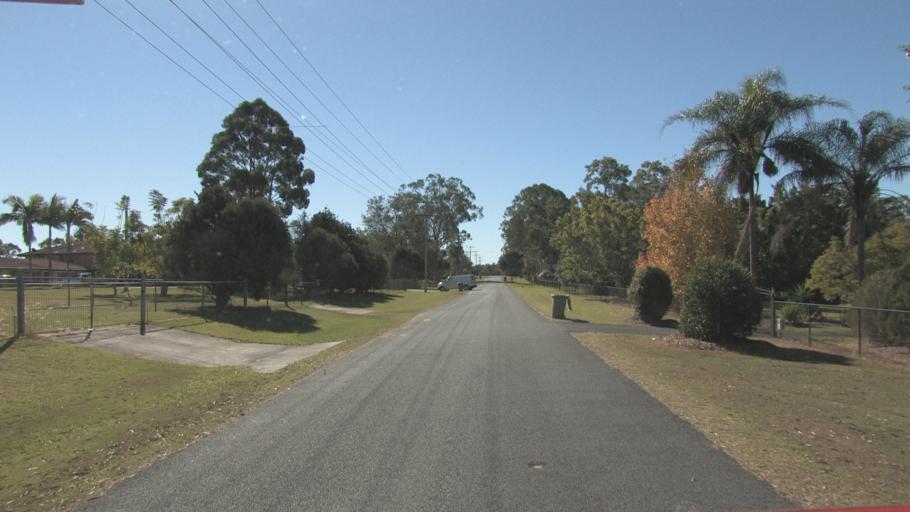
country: AU
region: Queensland
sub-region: Logan
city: Park Ridge South
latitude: -27.7260
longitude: 153.0393
